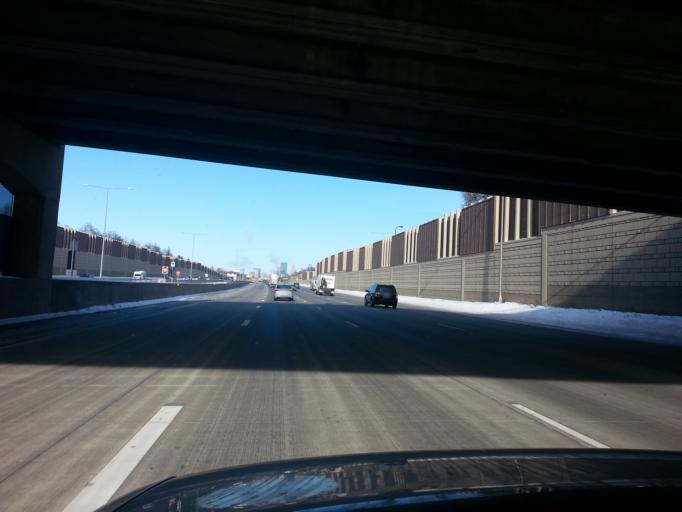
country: US
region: Minnesota
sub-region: Hennepin County
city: Richfield
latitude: 44.9194
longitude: -93.2746
